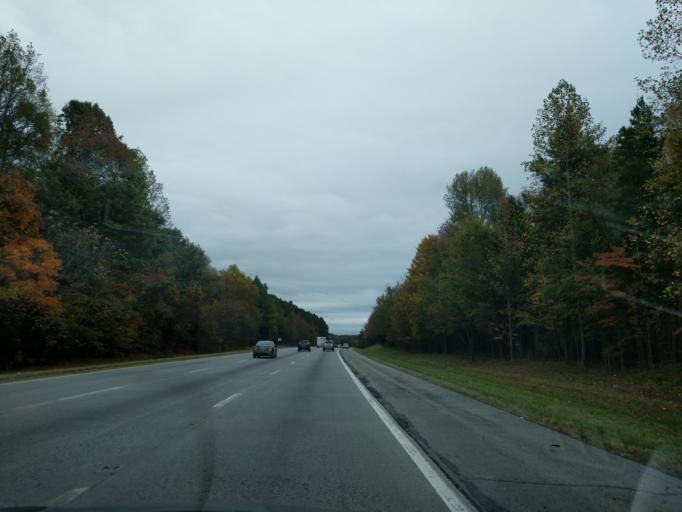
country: US
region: North Carolina
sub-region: Davidson County
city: Lexington
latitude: 35.8215
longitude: -80.1704
